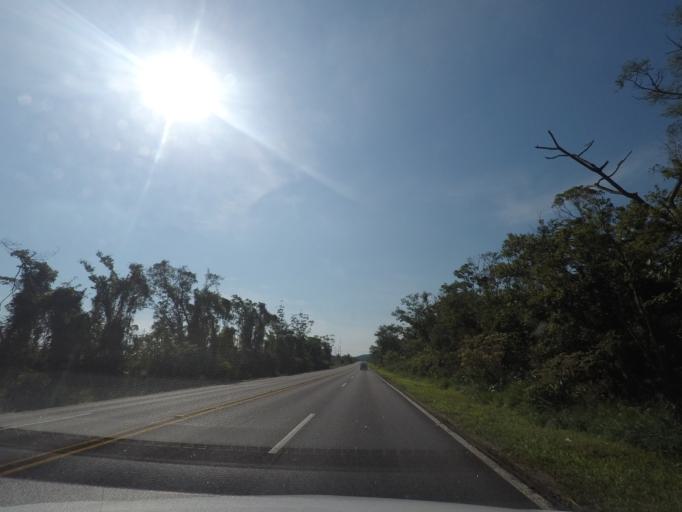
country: BR
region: Parana
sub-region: Paranagua
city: Paranagua
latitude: -25.5870
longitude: -48.6116
